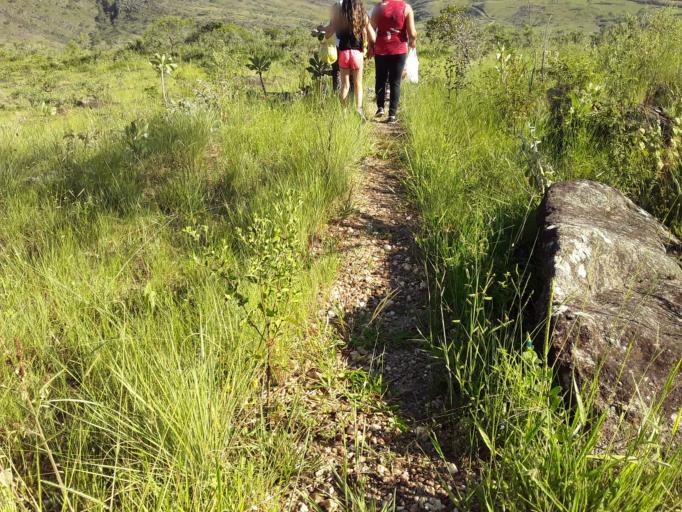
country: BR
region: Minas Gerais
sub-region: Sao Joao Del Rei
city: Sao Joao del Rei
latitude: -21.1275
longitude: -44.2755
